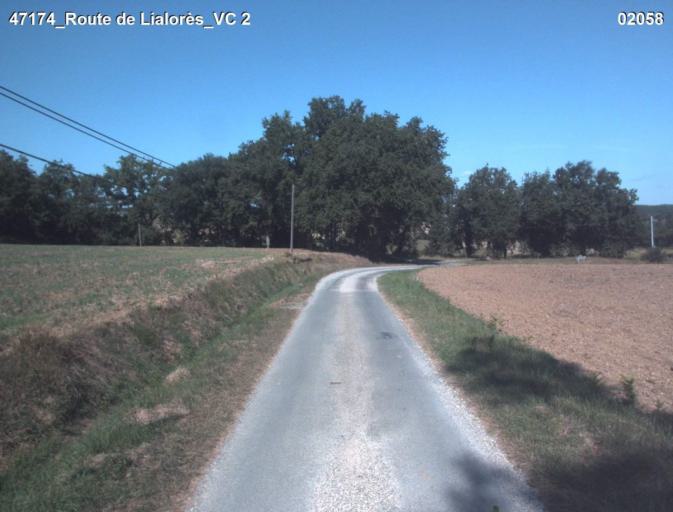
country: FR
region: Midi-Pyrenees
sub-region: Departement du Gers
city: Condom
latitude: 44.0219
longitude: 0.3697
